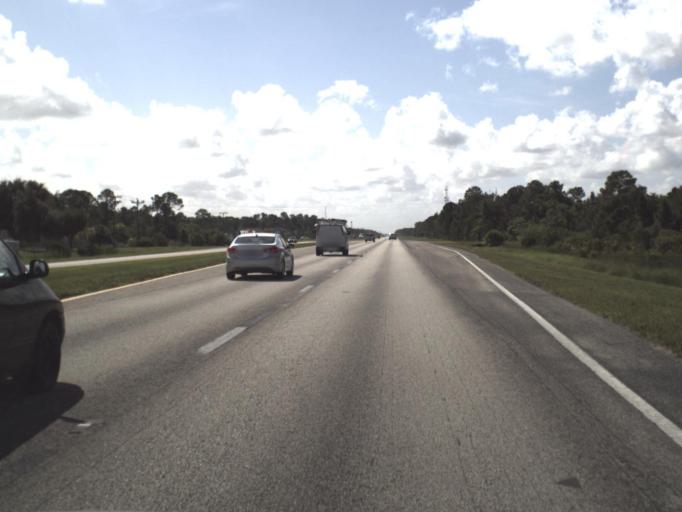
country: US
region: Florida
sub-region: Charlotte County
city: Charlotte Park
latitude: 26.8517
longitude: -81.9838
